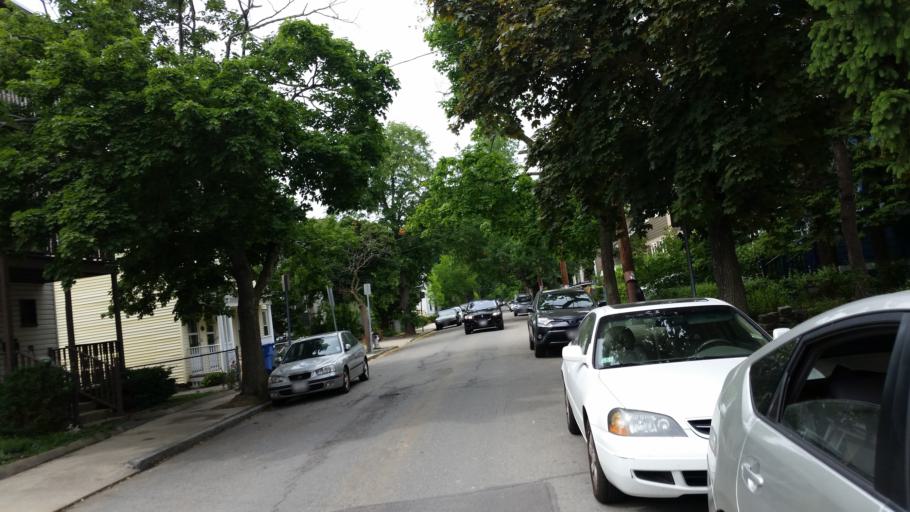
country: US
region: Massachusetts
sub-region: Middlesex County
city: Arlington
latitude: 42.3942
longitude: -71.1321
